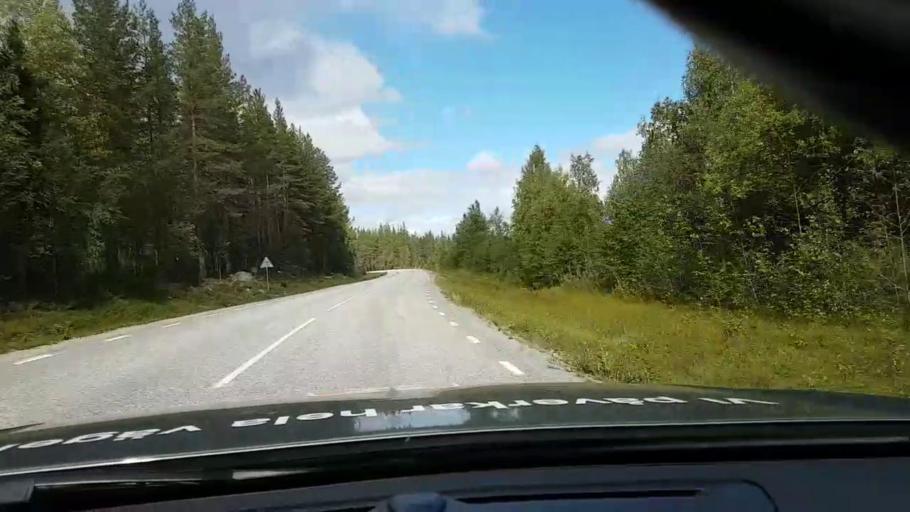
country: SE
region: Vaesternorrland
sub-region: OErnskoeldsviks Kommun
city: Bredbyn
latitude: 63.6877
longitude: 17.7705
